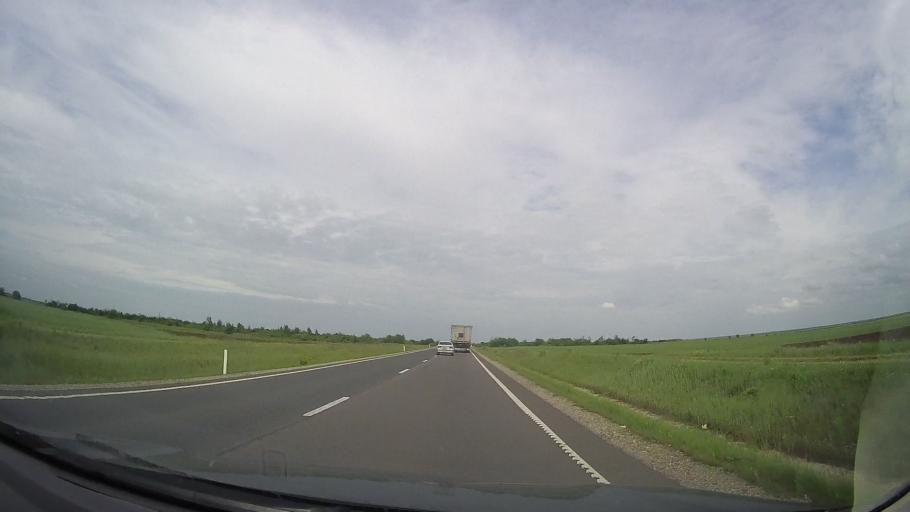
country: RO
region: Teleorman
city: Alexandria
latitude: 43.9929
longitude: 25.3389
